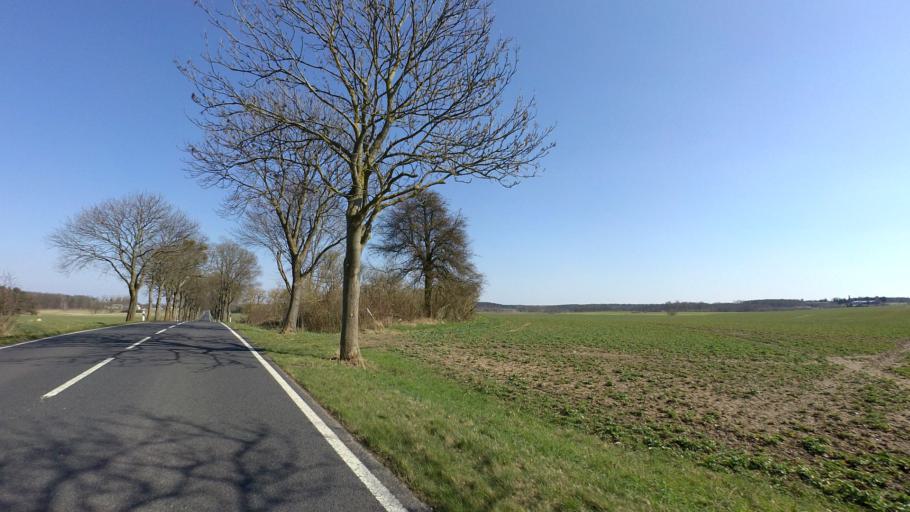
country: DE
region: Brandenburg
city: Sonnenberg
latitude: 53.0048
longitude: 13.0979
